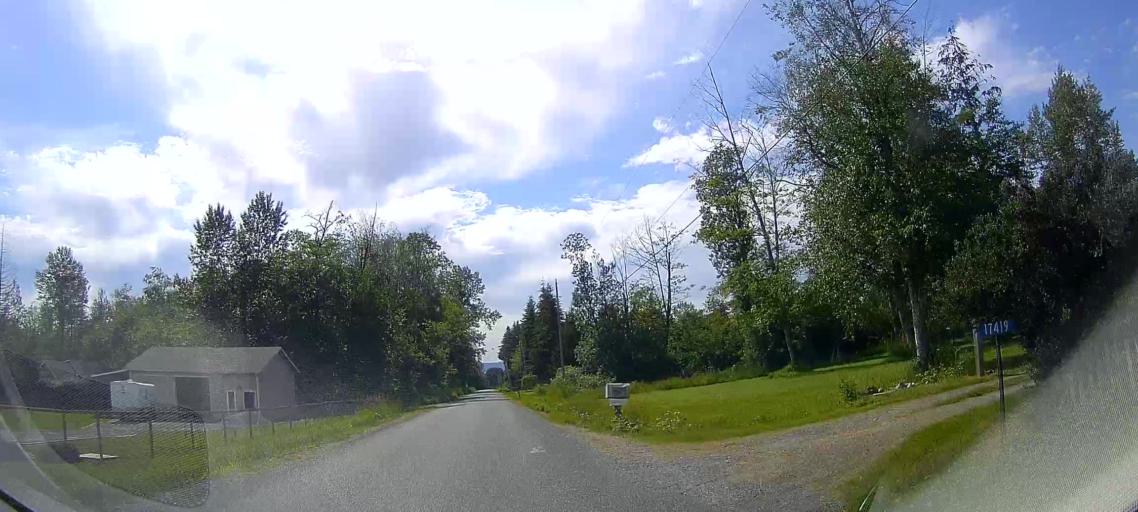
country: US
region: Washington
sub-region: Skagit County
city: Burlington
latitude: 48.5448
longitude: -122.3699
